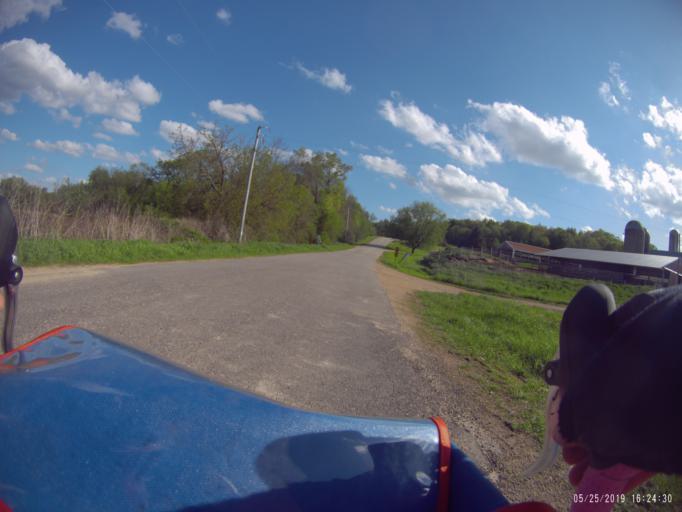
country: US
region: Wisconsin
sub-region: Dane County
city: Mount Horeb
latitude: 42.9524
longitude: -89.7017
